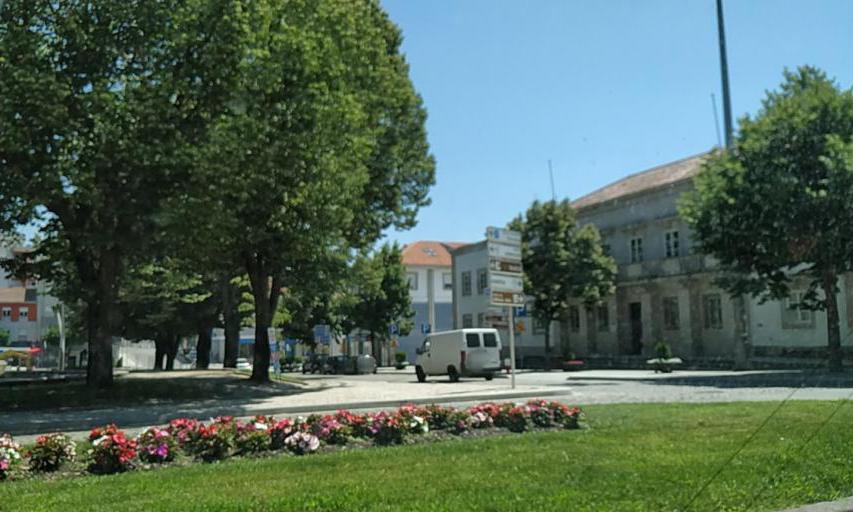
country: PT
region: Braganca
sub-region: Braganca Municipality
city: Braganca
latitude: 41.8068
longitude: -6.7596
